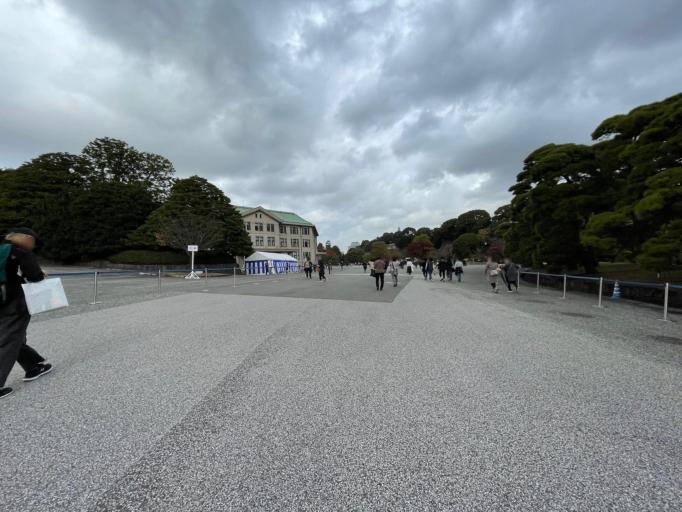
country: JP
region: Tokyo
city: Tokyo
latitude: 35.6832
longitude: 139.7552
